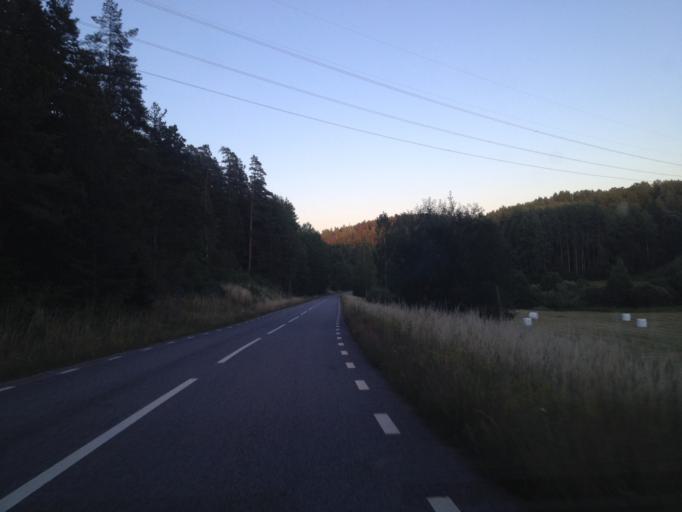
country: SE
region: Kalmar
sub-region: Vasterviks Kommun
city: Overum
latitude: 58.0228
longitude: 16.1273
